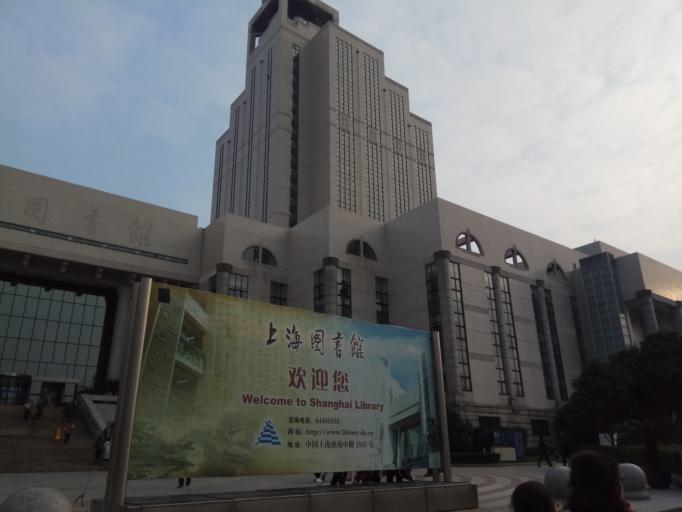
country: CN
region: Shanghai Shi
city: Xuhui
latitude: 31.2100
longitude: 121.4401
